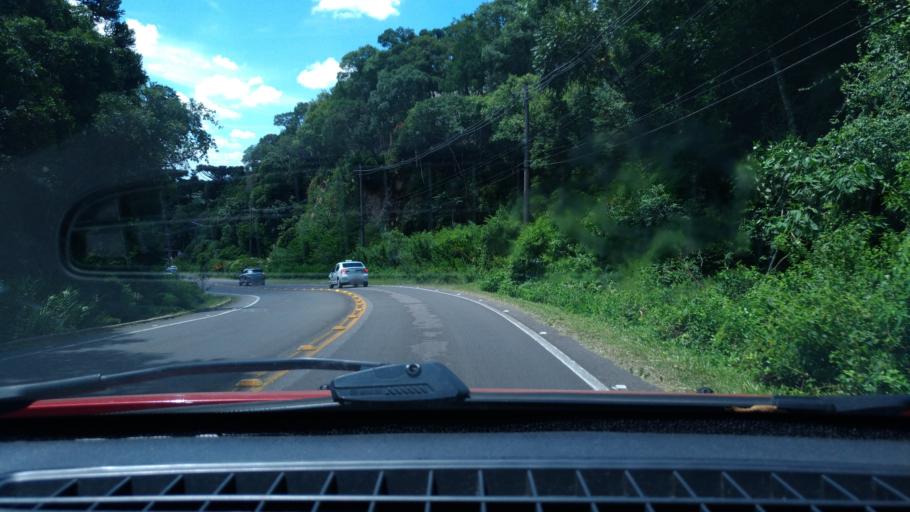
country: BR
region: Rio Grande do Sul
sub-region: Canela
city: Canela
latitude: -29.3522
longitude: -50.8325
